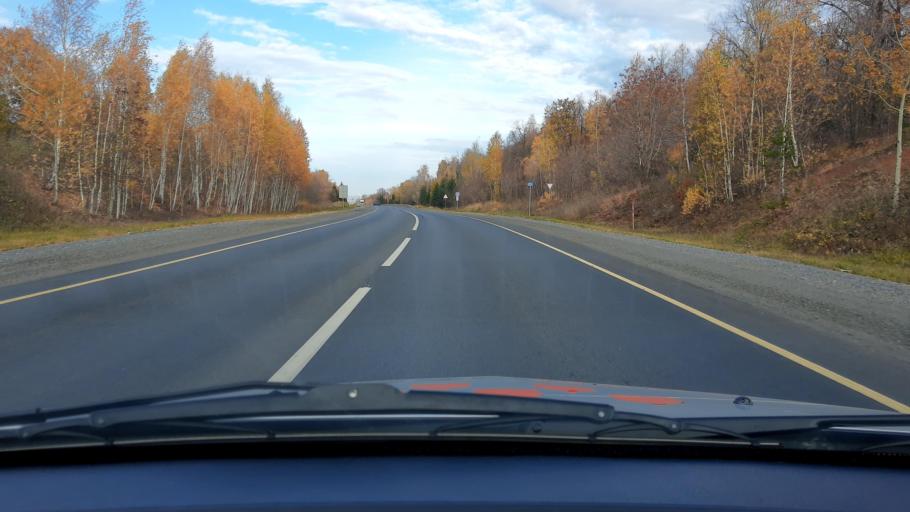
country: RU
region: Bashkortostan
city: Avdon
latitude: 54.8348
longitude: 55.7232
